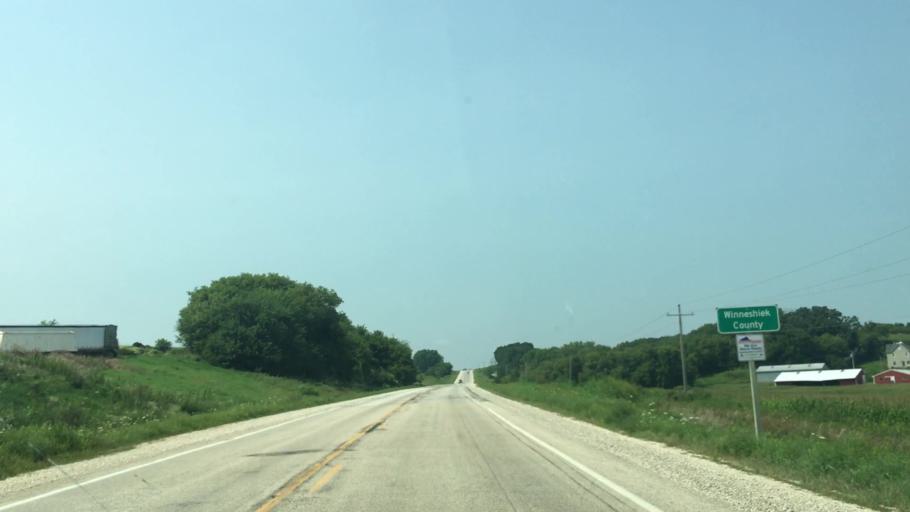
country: US
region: Iowa
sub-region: Fayette County
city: West Union
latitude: 43.0821
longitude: -91.8445
